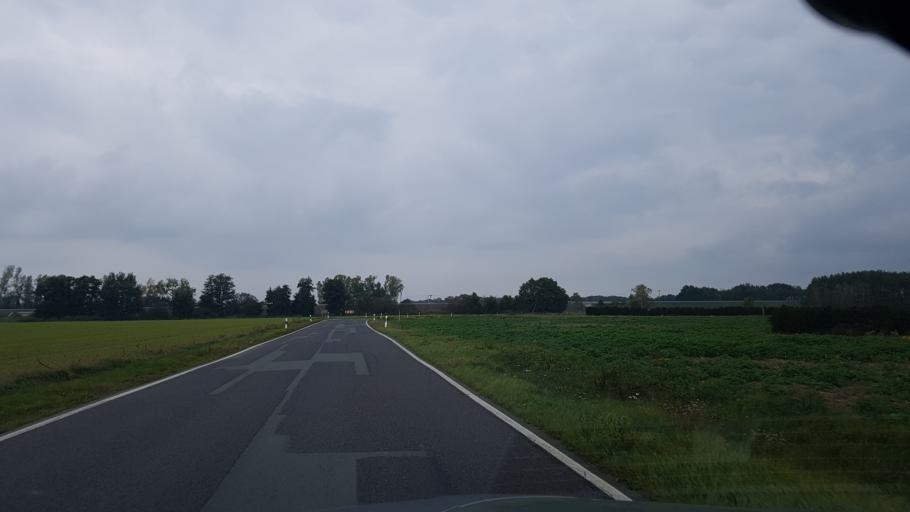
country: DE
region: Brandenburg
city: Bad Liebenwerda
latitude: 51.4998
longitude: 13.4053
